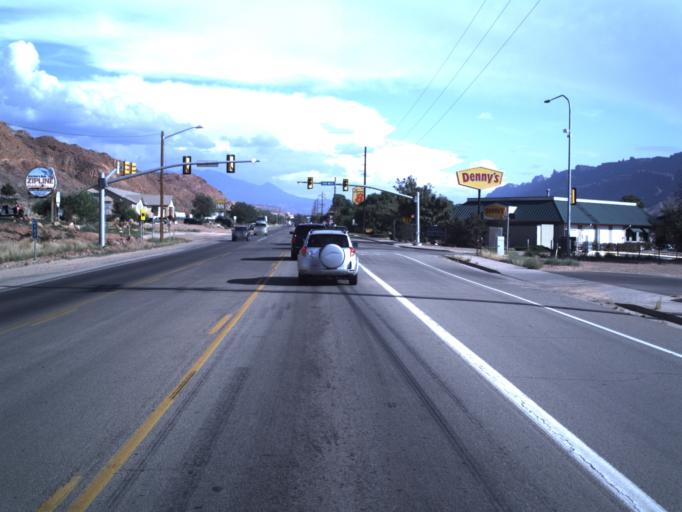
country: US
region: Utah
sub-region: Grand County
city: Moab
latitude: 38.5893
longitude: -109.5615
